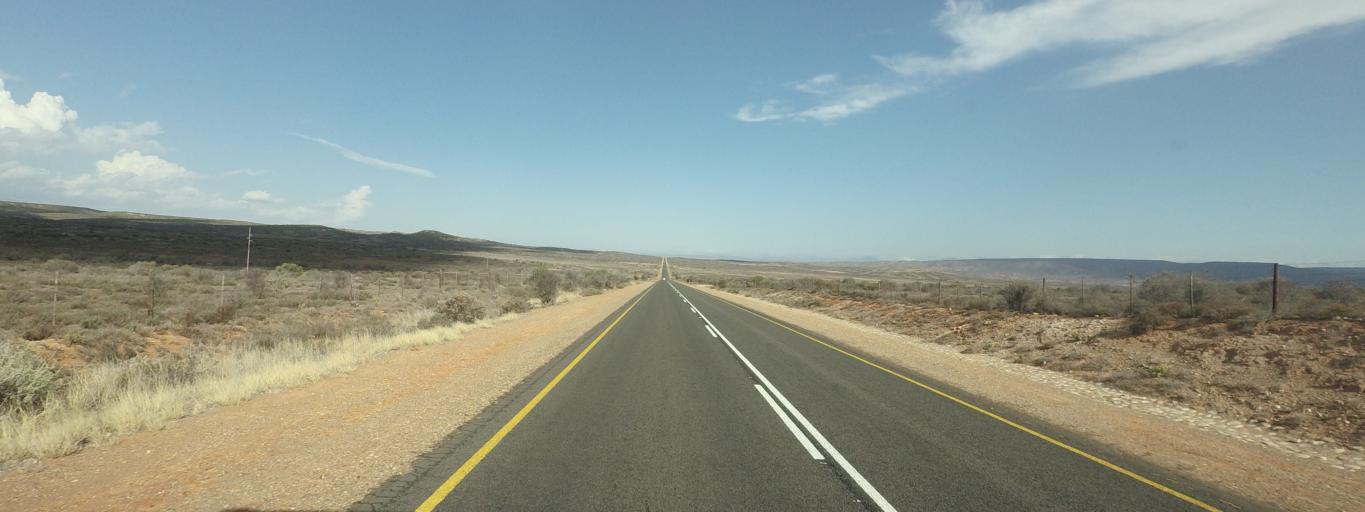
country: ZA
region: Western Cape
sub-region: Eden District Municipality
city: Oudtshoorn
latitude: -33.5788
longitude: 21.9696
